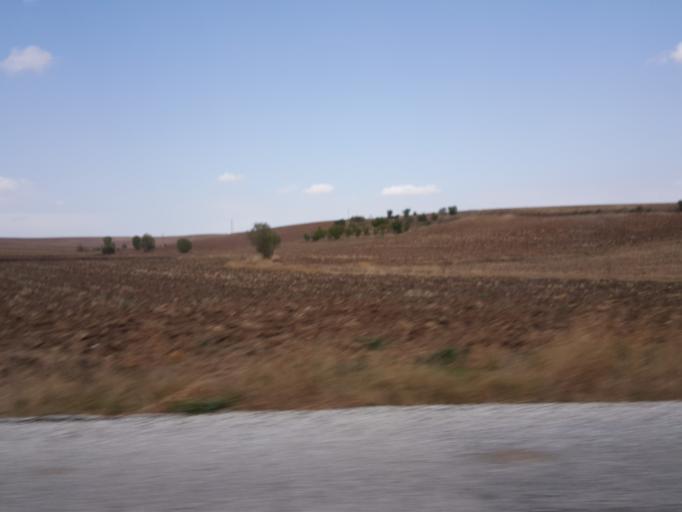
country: TR
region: Corum
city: Alaca
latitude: 40.1549
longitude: 34.7319
